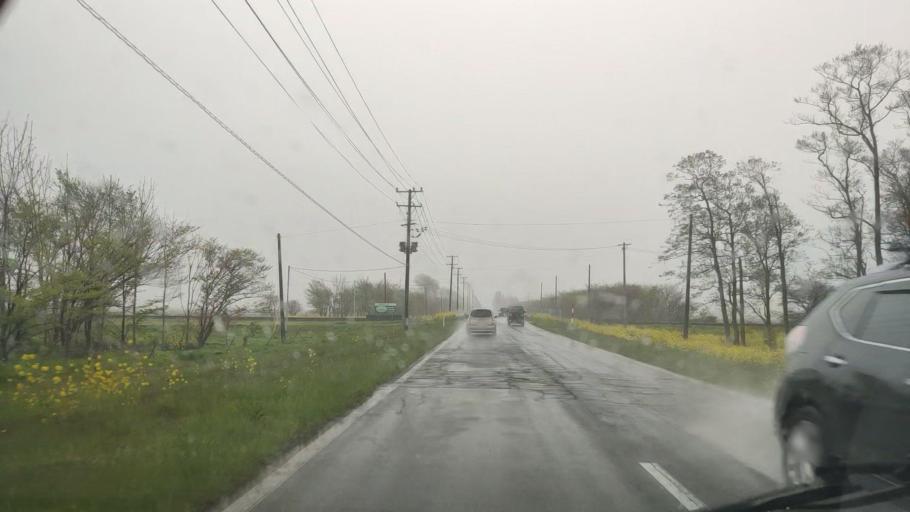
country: JP
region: Akita
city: Tenno
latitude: 39.9829
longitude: 139.9463
